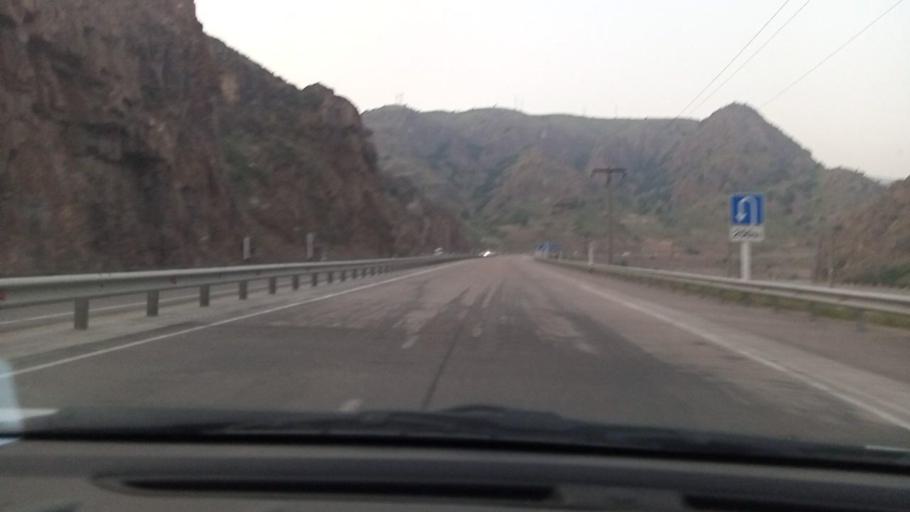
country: UZ
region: Toshkent
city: Angren
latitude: 41.1305
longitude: 70.3712
